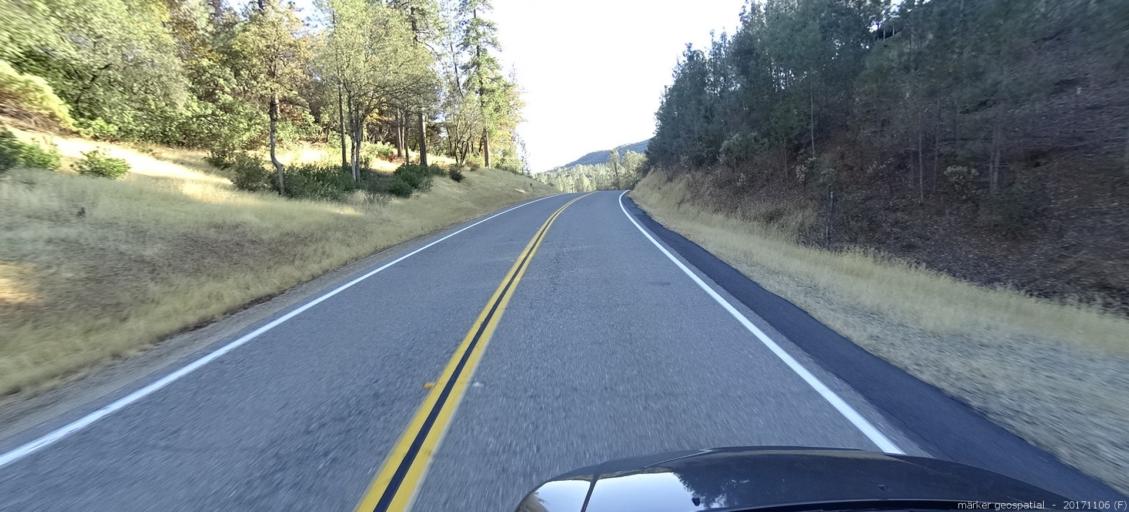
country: US
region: California
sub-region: Shasta County
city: Shasta
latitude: 40.5811
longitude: -122.4811
